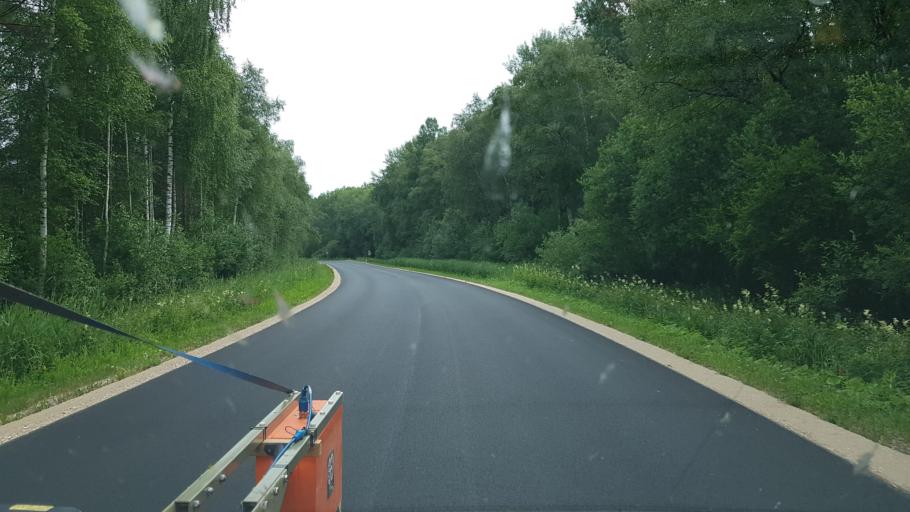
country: EE
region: Paernumaa
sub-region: Audru vald
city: Audru
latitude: 58.6214
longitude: 24.2420
